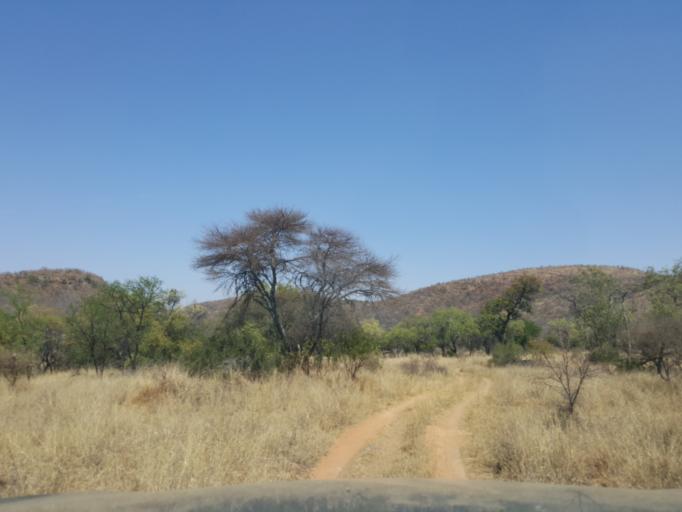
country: BW
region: South East
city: Lobatse
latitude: -25.1412
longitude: 25.6707
